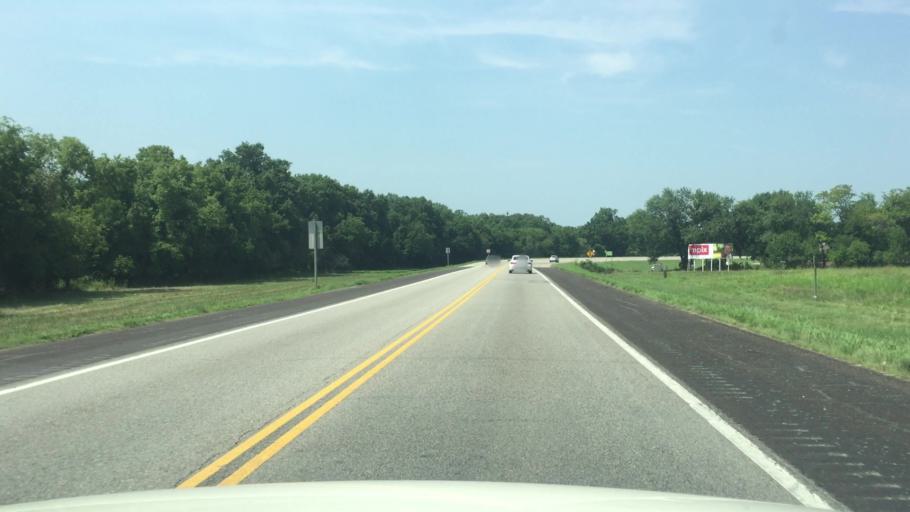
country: US
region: Kansas
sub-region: Crawford County
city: Pittsburg
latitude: 37.4056
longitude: -94.7238
